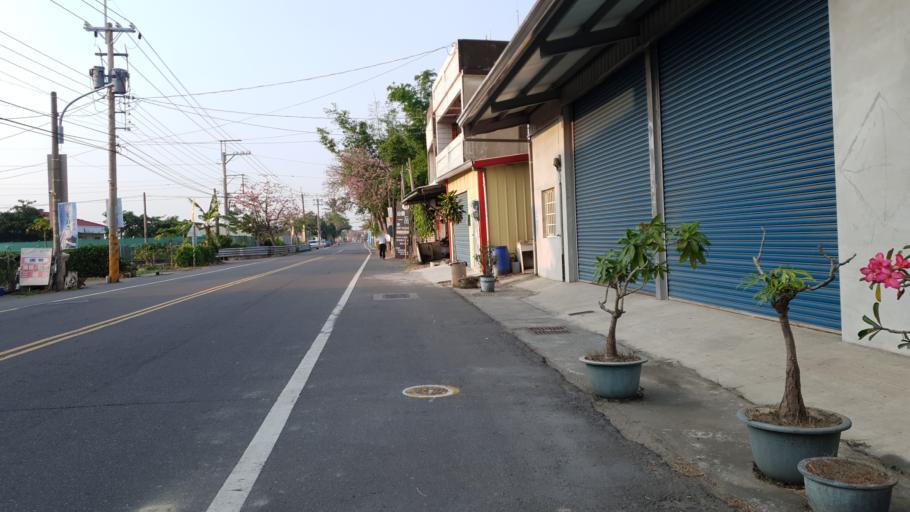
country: TW
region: Taiwan
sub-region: Yunlin
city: Douliu
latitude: 23.7572
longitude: 120.4195
